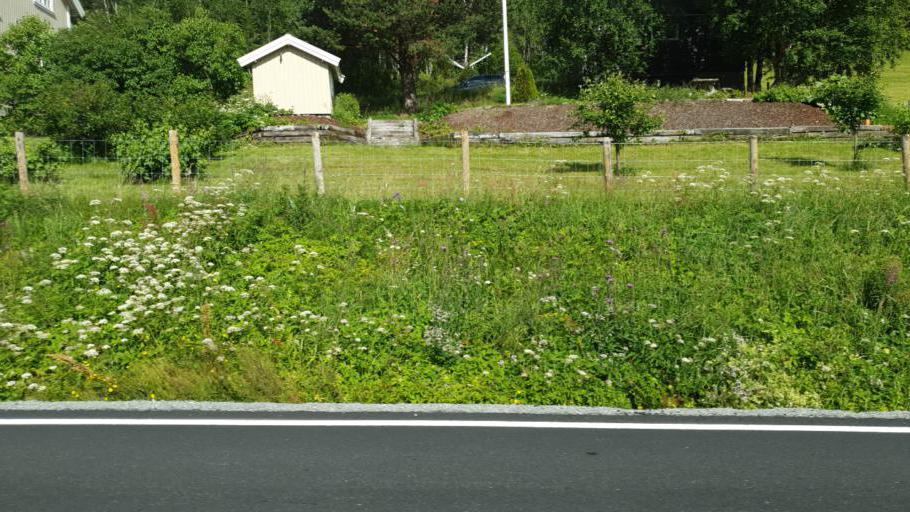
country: NO
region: Oppland
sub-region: Oystre Slidre
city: Heggenes
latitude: 61.1695
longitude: 8.9951
